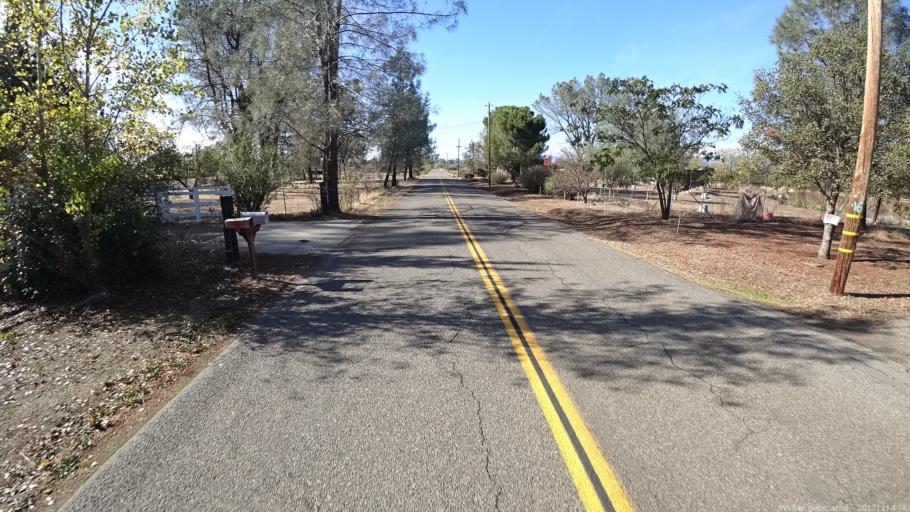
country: US
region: California
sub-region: Shasta County
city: Anderson
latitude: 40.4320
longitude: -122.4206
